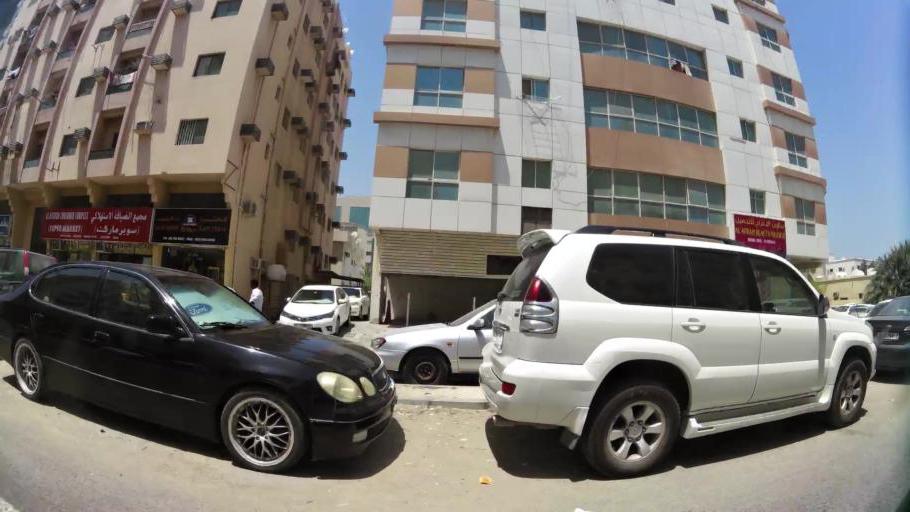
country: AE
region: Ajman
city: Ajman
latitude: 25.4010
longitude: 55.4481
